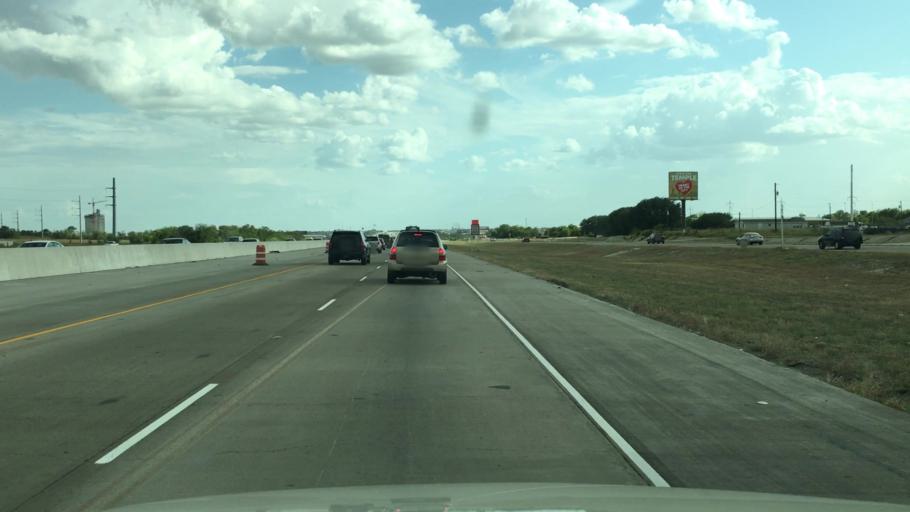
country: US
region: Texas
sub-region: Bell County
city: Troy
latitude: 31.1659
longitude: -97.3199
